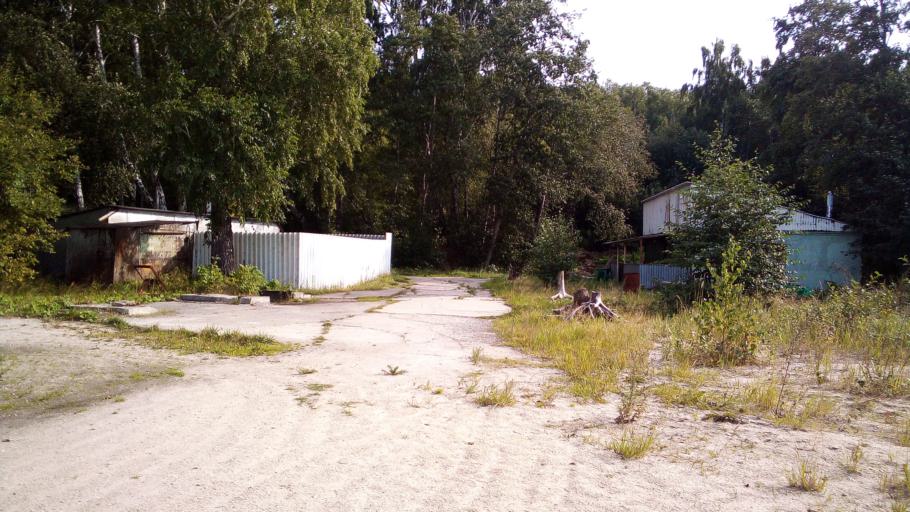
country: RU
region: Chelyabinsk
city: Tayginka
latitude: 55.4754
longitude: 60.4888
